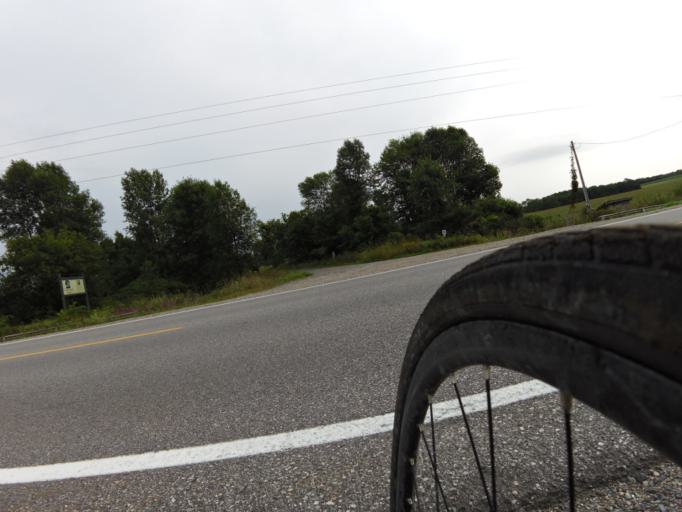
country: CA
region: Ontario
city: Perth
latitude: 44.6239
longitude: -76.2450
